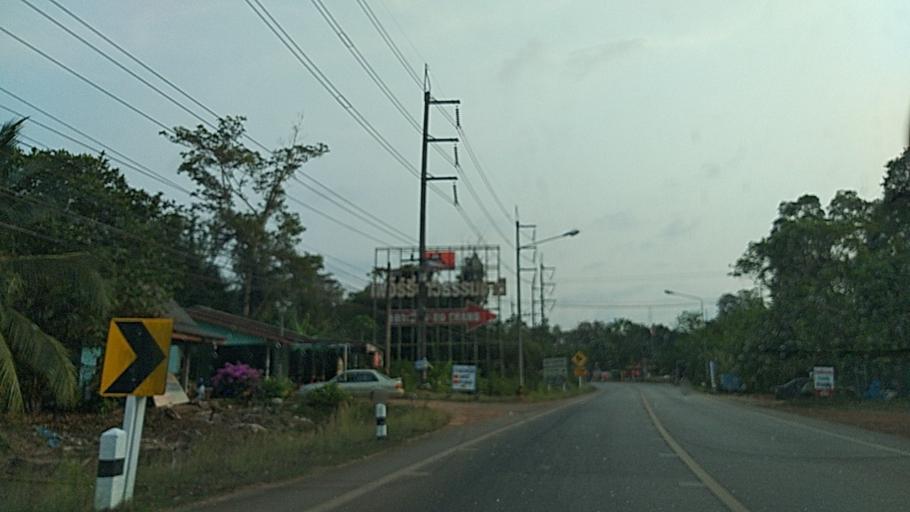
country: TH
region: Trat
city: Laem Ngop
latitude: 12.2188
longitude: 102.3081
